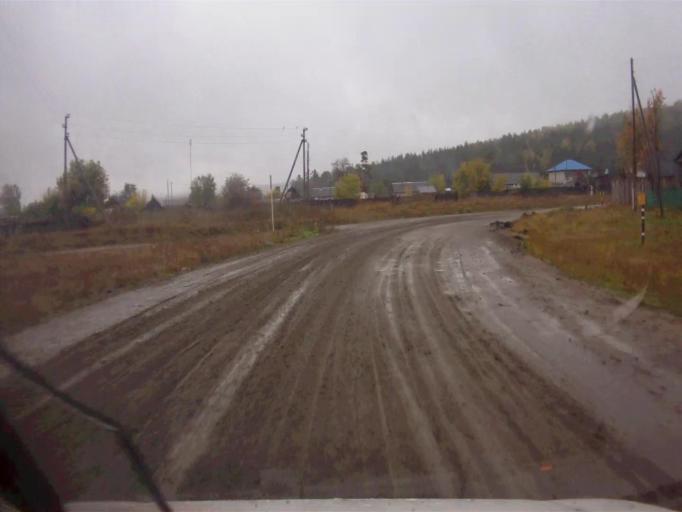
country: RU
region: Chelyabinsk
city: Kyshtym
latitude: 55.9023
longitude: 60.4657
